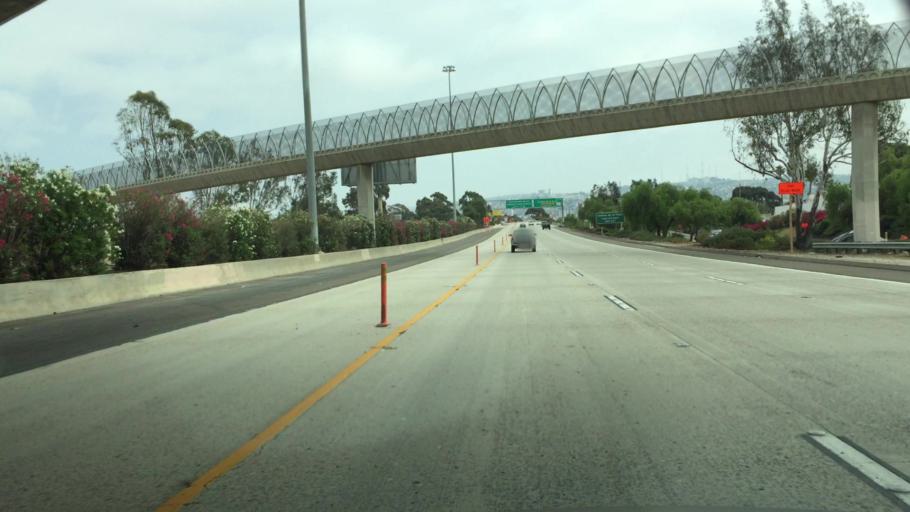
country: MX
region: Baja California
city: Tijuana
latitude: 32.5549
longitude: -117.0420
